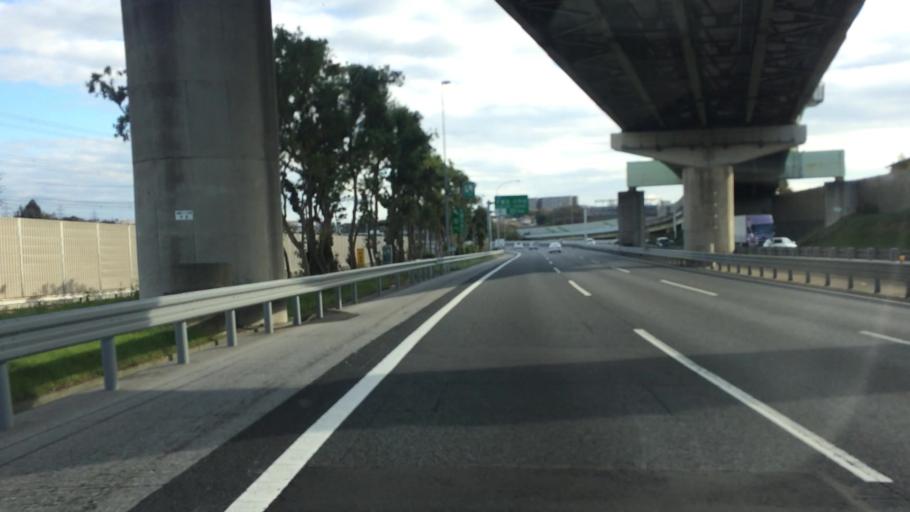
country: JP
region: Chiba
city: Yotsukaido
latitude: 35.6648
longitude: 140.1063
